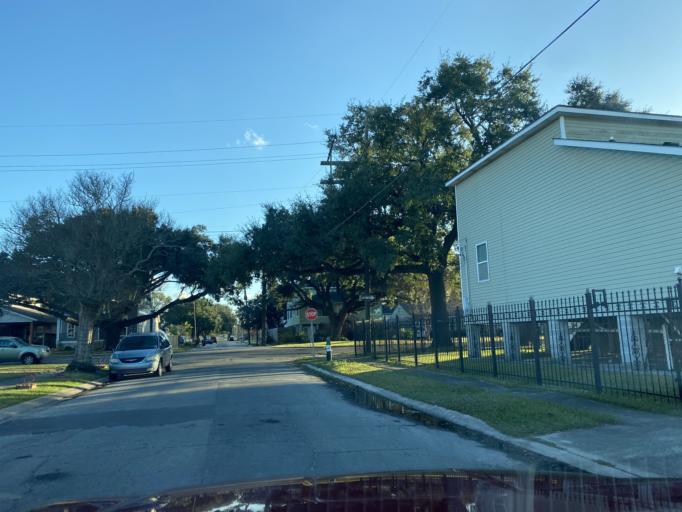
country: US
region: Louisiana
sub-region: Orleans Parish
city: New Orleans
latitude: 30.0176
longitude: -90.0537
